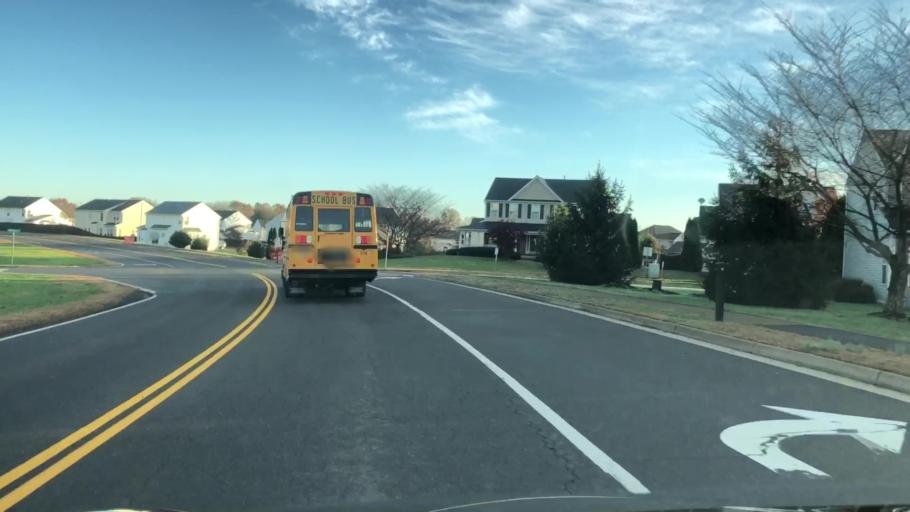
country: US
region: Virginia
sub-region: Fauquier County
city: Bealeton
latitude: 38.5776
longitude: -77.7604
